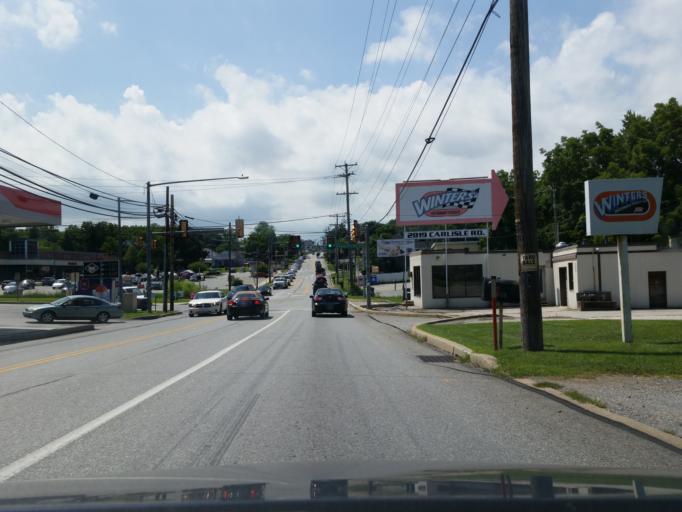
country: US
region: Pennsylvania
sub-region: York County
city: Weigelstown
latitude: 39.9817
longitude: -76.8123
